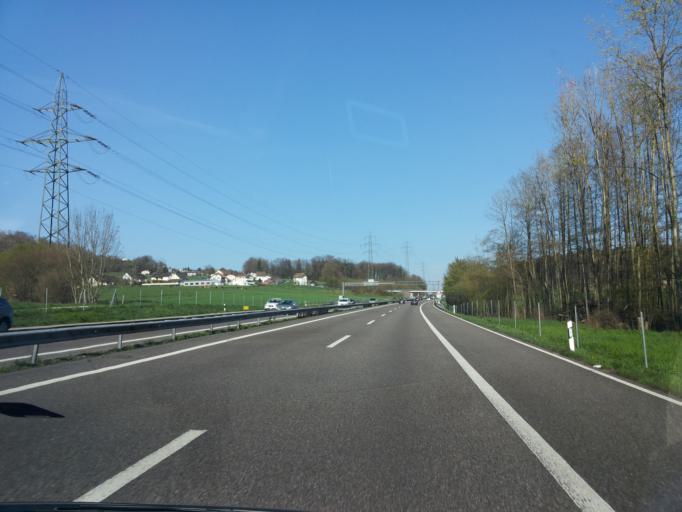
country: CH
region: Aargau
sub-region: Bezirk Zofingen
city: Safenwil
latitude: 47.3203
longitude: 7.9578
